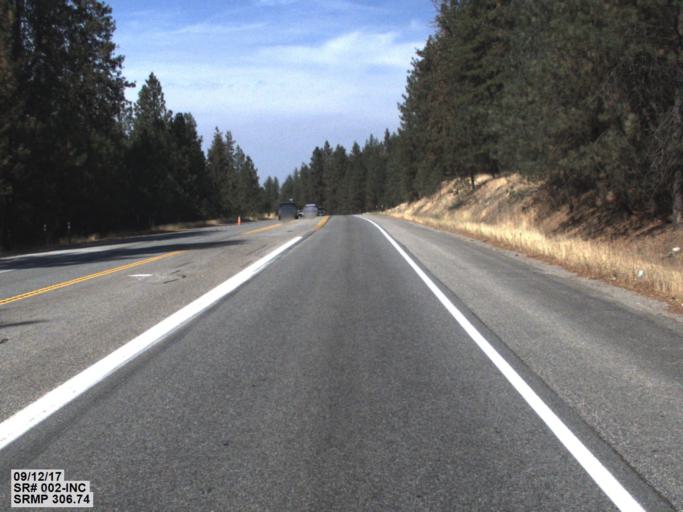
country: US
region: Washington
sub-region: Spokane County
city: Deer Park
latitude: 47.9219
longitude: -117.3501
